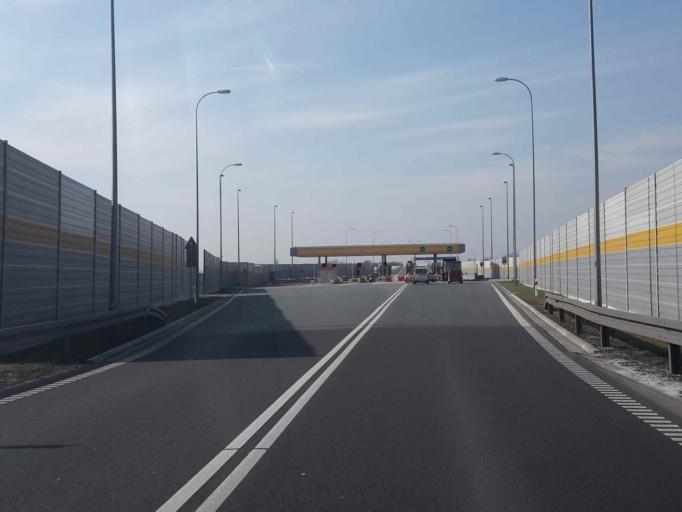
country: PL
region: Kujawsko-Pomorskie
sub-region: Powiat torunski
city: Lubicz Dolny
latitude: 53.0936
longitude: 18.7576
